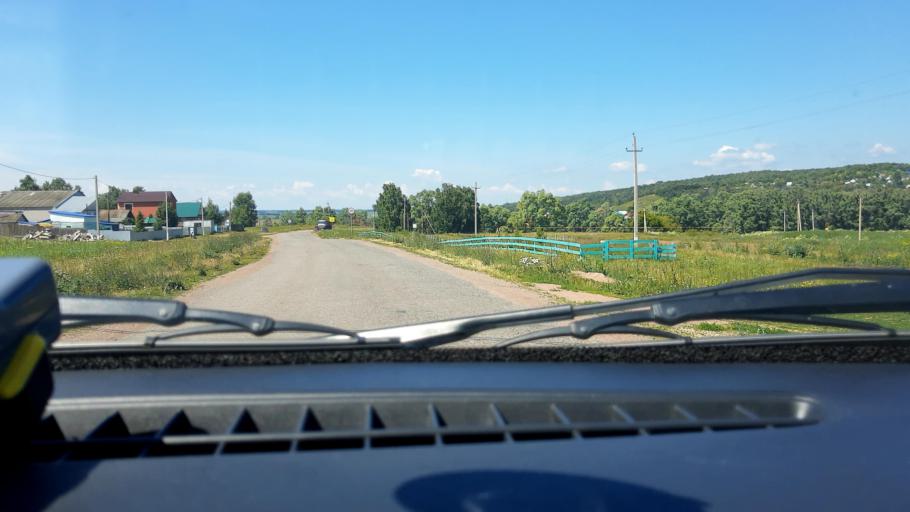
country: RU
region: Bashkortostan
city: Karmaskaly
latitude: 54.3569
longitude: 55.9077
